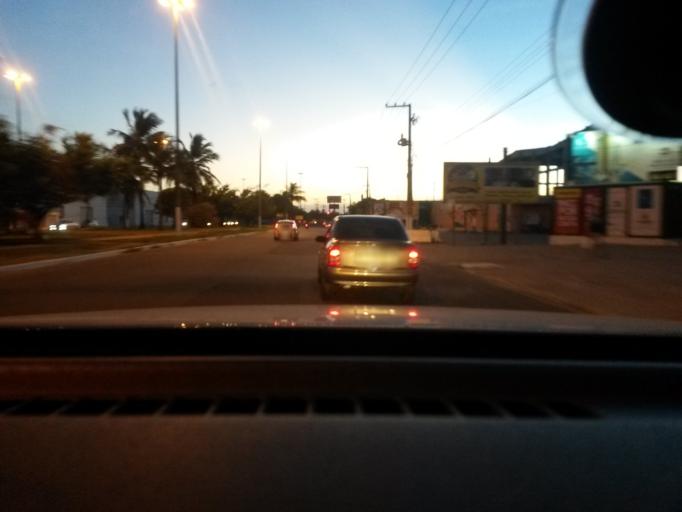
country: BR
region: Sergipe
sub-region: Aracaju
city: Aracaju
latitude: -10.9929
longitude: -37.0630
